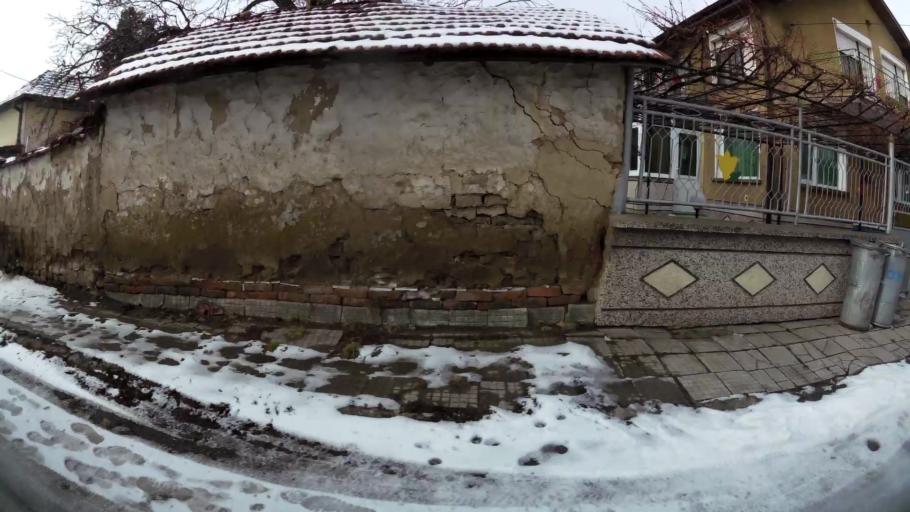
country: BG
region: Sofia-Capital
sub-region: Stolichna Obshtina
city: Sofia
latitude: 42.7138
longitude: 23.4084
